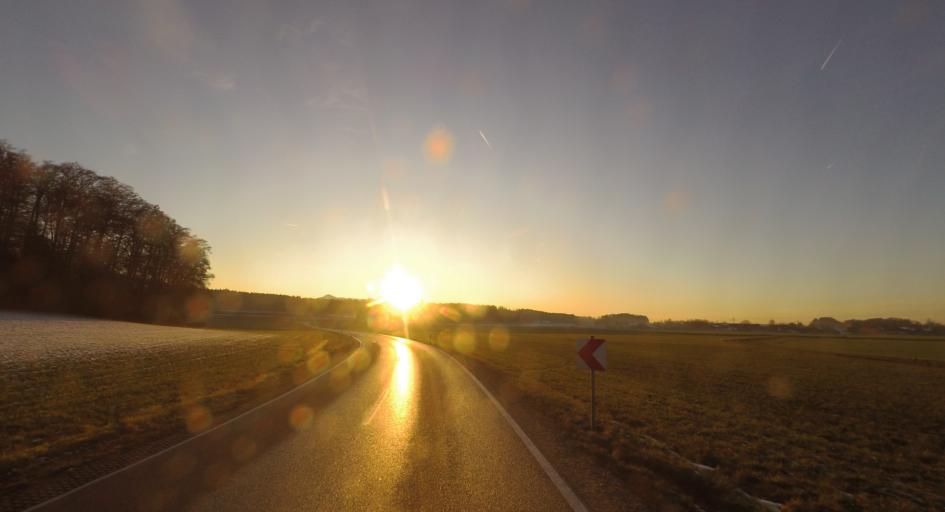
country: DE
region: Bavaria
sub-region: Upper Bavaria
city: Nussdorf
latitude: 47.8871
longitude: 12.5857
